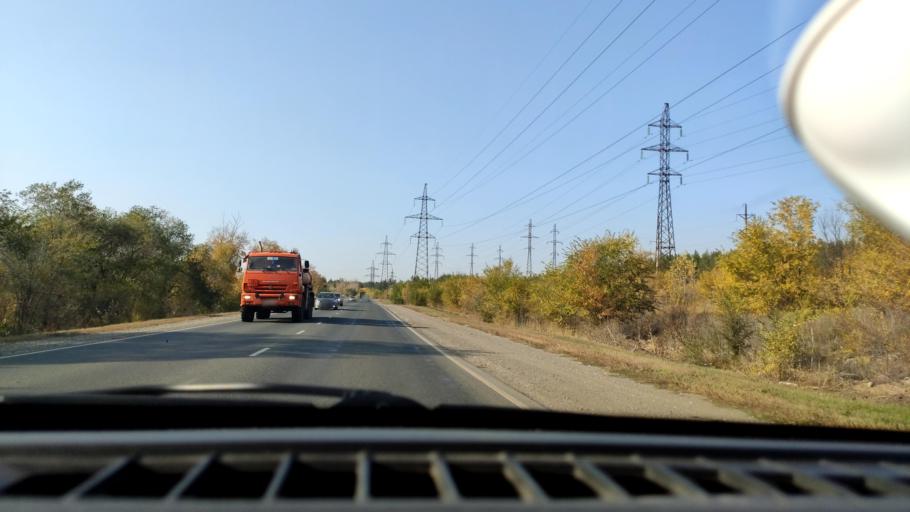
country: RU
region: Samara
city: Samara
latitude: 53.1196
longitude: 50.2168
